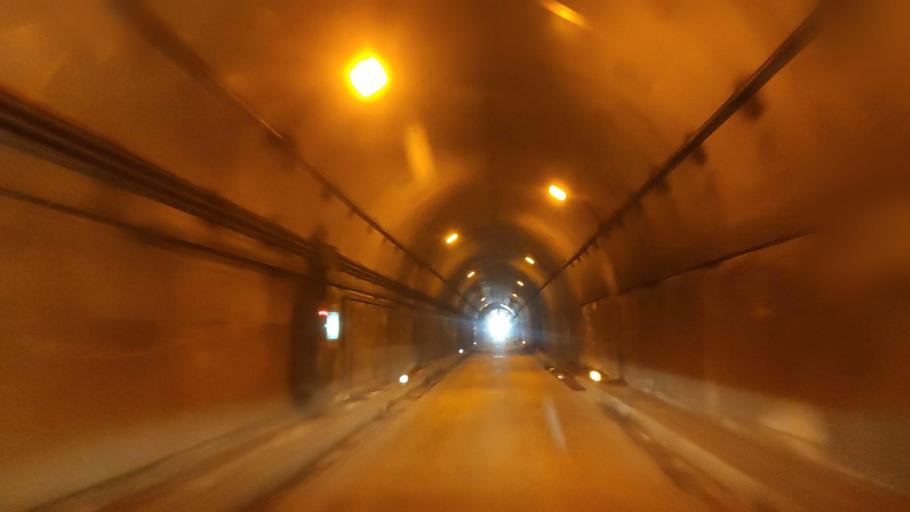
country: JP
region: Gifu
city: Gifu-shi
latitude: 35.4214
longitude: 136.7709
